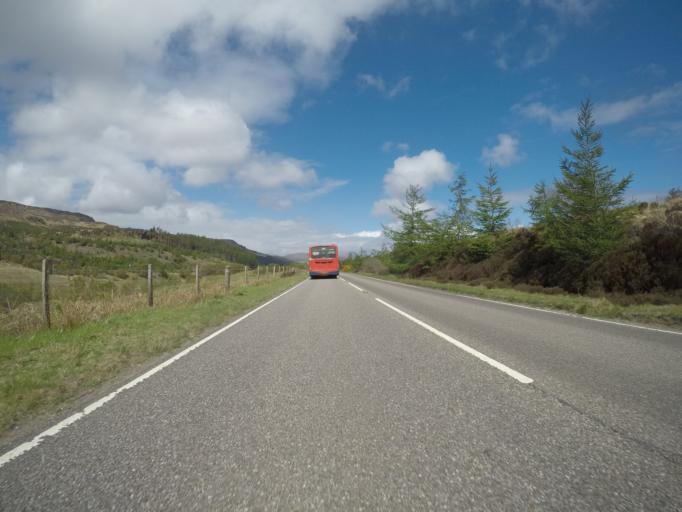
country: GB
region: Scotland
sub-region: Highland
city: Portree
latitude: 57.3697
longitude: -6.1940
